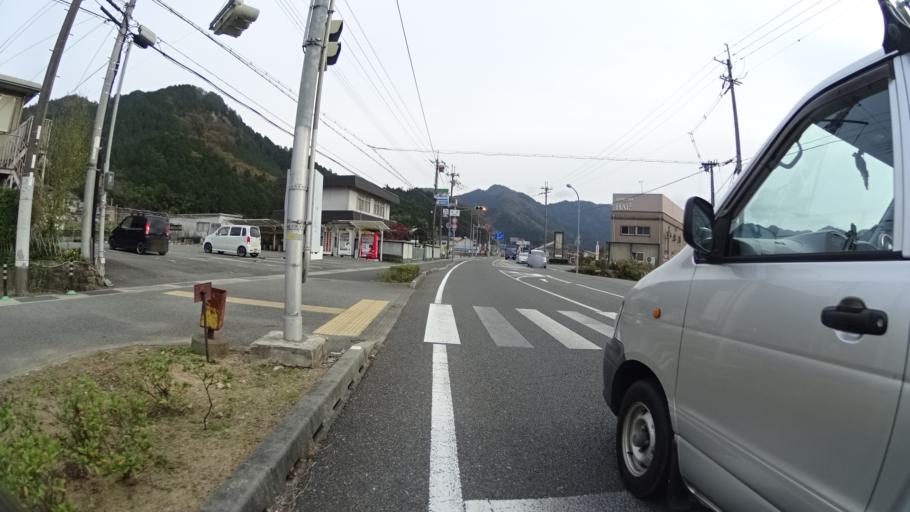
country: JP
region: Hyogo
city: Sasayama
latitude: 35.1221
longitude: 135.0857
